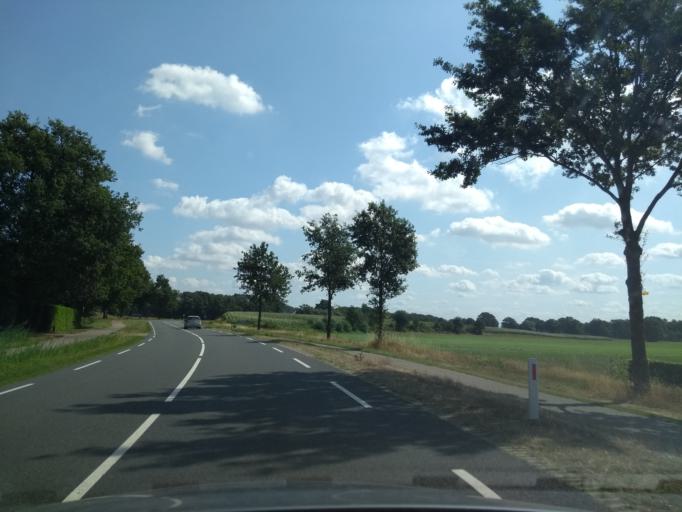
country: DE
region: Lower Saxony
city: Lage
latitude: 52.4060
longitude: 6.9267
